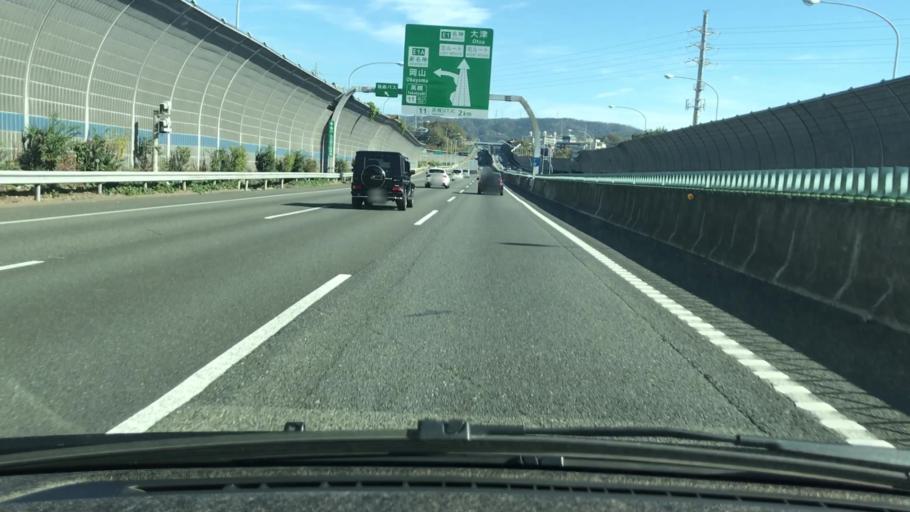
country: JP
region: Osaka
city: Takatsuki
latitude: 34.8599
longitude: 135.6002
